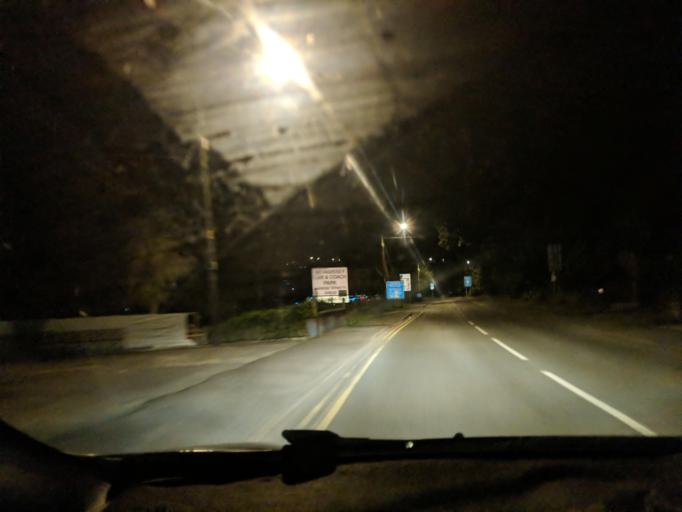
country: GB
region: England
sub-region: Cornwall
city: Mevagissey
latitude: 50.2731
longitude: -4.7914
